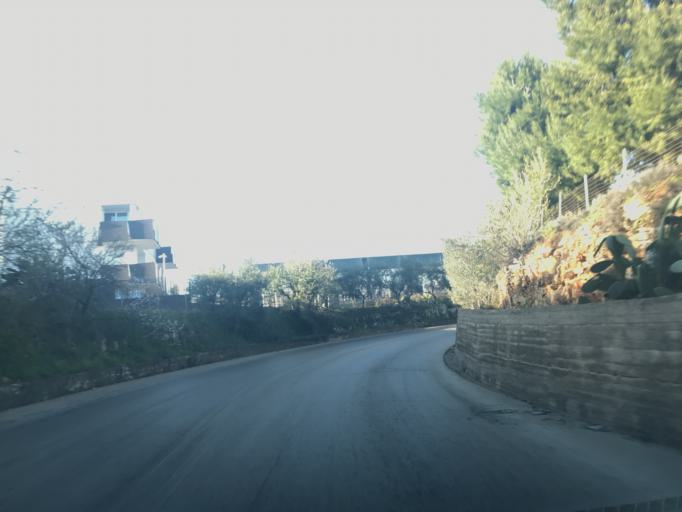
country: IT
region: Apulia
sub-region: Provincia di Bari
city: Corato
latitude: 41.1350
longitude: 16.4150
